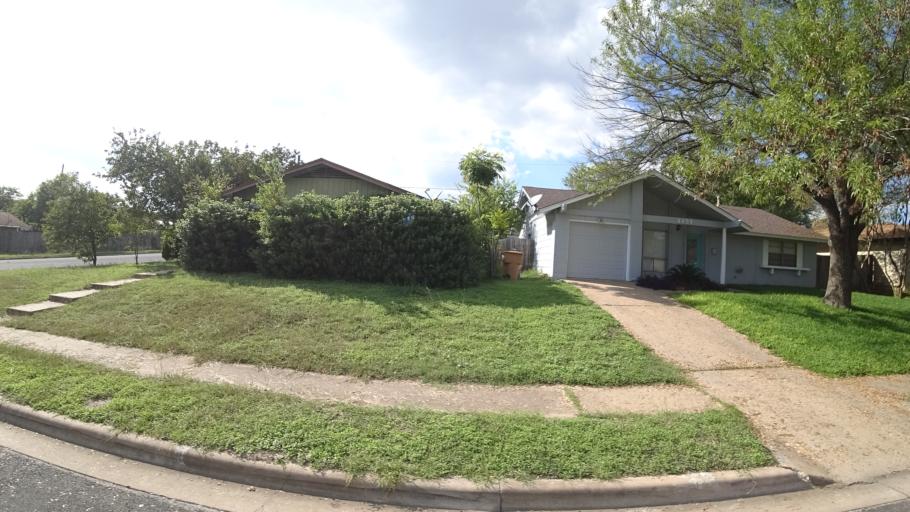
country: US
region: Texas
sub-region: Travis County
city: Austin
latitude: 30.3554
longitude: -97.7124
